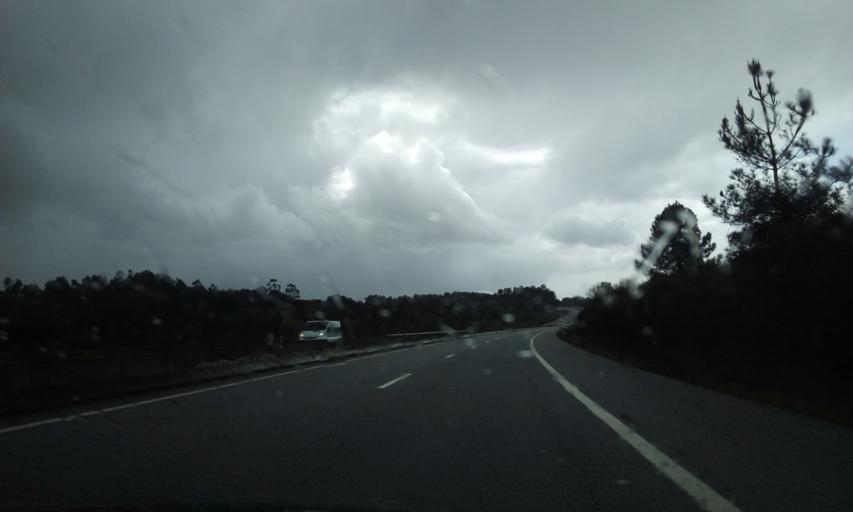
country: PT
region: Viseu
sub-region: Viseu
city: Viseu
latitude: 40.6292
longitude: -7.8915
